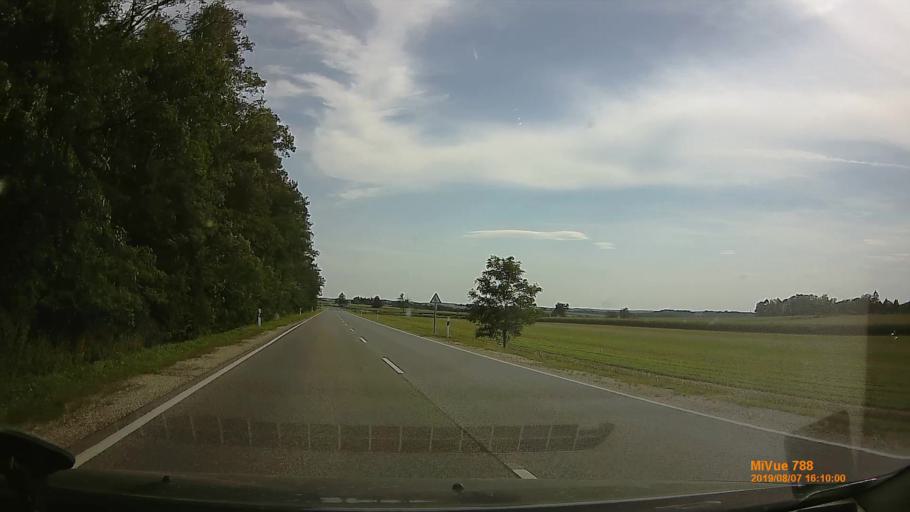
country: HU
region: Zala
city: Zalalovo
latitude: 46.8853
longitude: 16.5998
